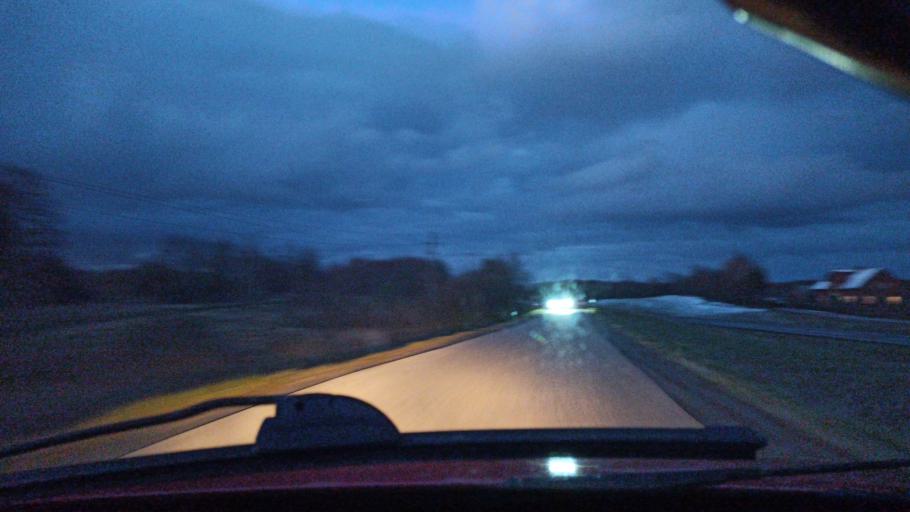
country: PL
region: Warmian-Masurian Voivodeship
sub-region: Powiat elblaski
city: Gronowo Gorne
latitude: 54.1734
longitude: 19.5355
